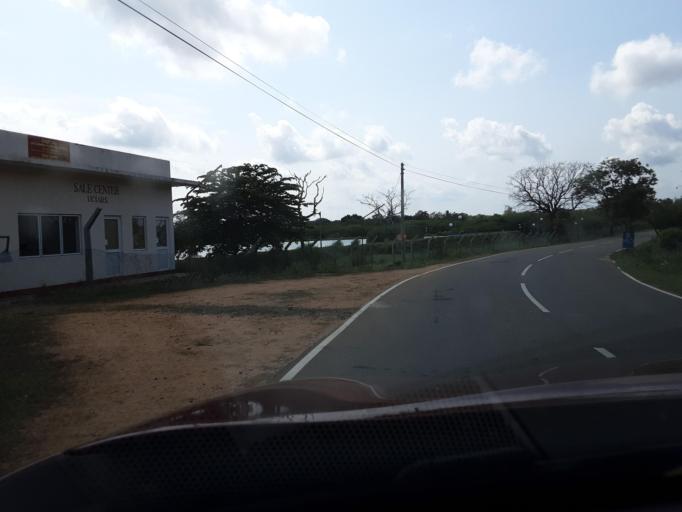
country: LK
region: Southern
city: Tangalla
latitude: 6.2084
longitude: 81.2060
